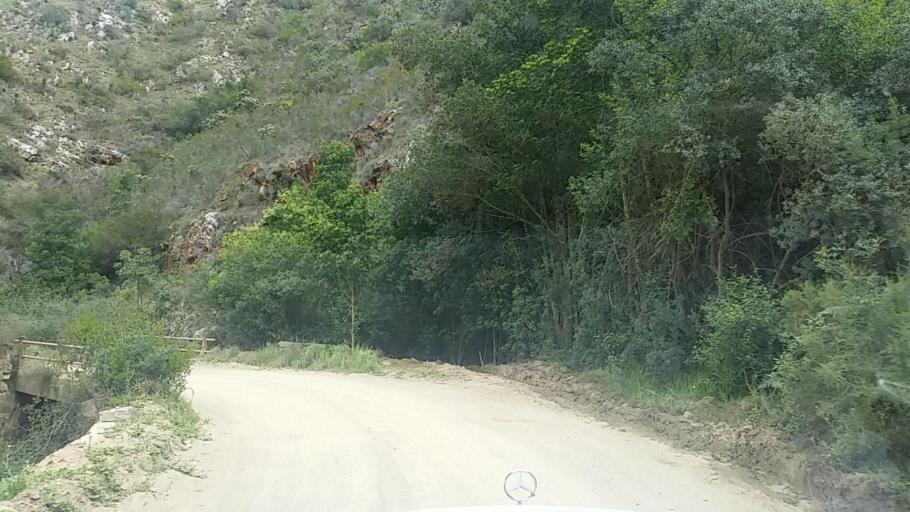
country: ZA
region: Western Cape
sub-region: Eden District Municipality
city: Knysna
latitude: -33.8005
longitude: 23.1782
